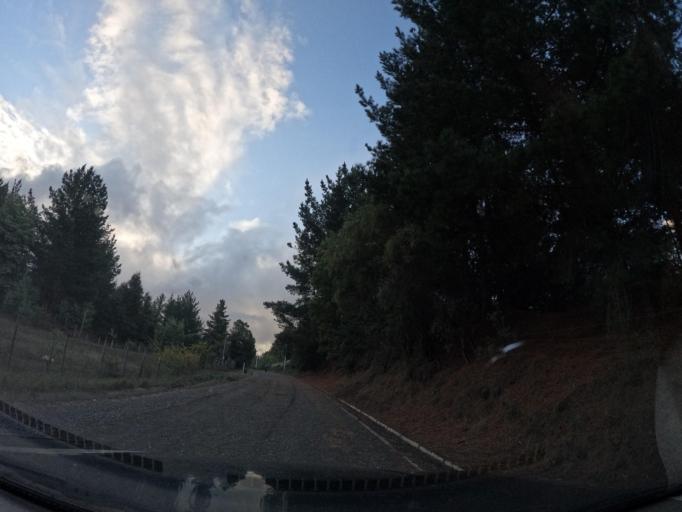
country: CL
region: Biobio
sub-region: Provincia de Concepcion
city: Chiguayante
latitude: -37.0596
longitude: -72.9527
